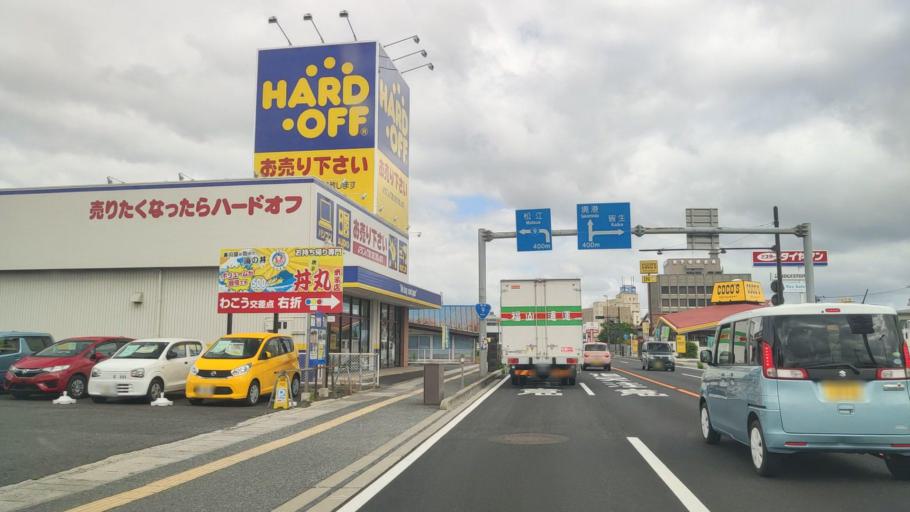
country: JP
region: Tottori
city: Yonago
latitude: 35.4366
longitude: 133.3455
